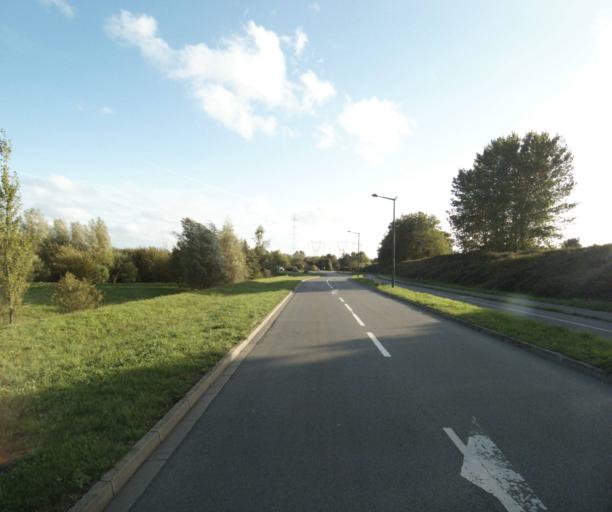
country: FR
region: Nord-Pas-de-Calais
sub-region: Departement du Nord
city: Sequedin
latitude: 50.6233
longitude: 2.9904
